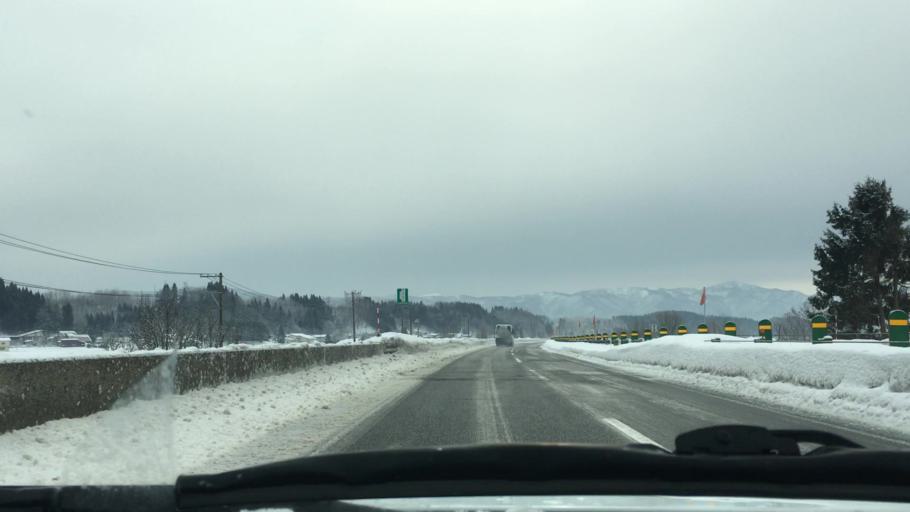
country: JP
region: Akita
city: Hanawa
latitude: 40.2978
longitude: 140.7517
